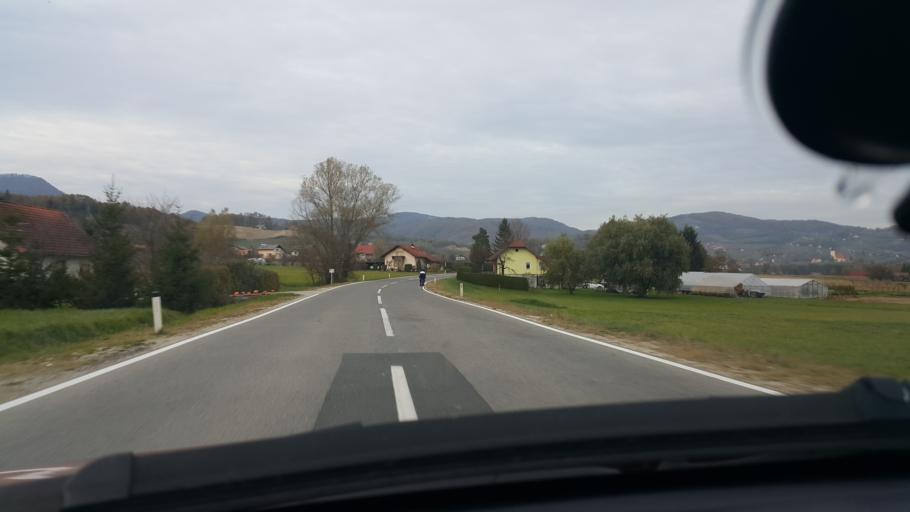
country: SI
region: Bistrica ob Sotli
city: Bistrica ob Sotli
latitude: 45.9988
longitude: 15.6934
